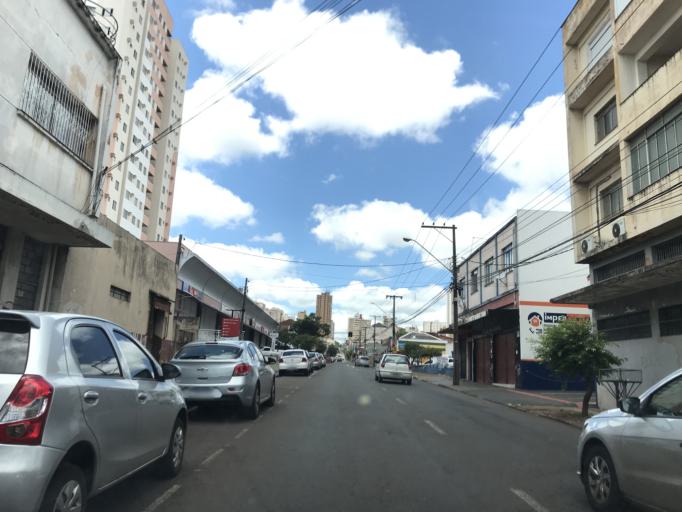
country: BR
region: Parana
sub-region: Londrina
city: Londrina
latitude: -23.3023
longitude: -51.1628
